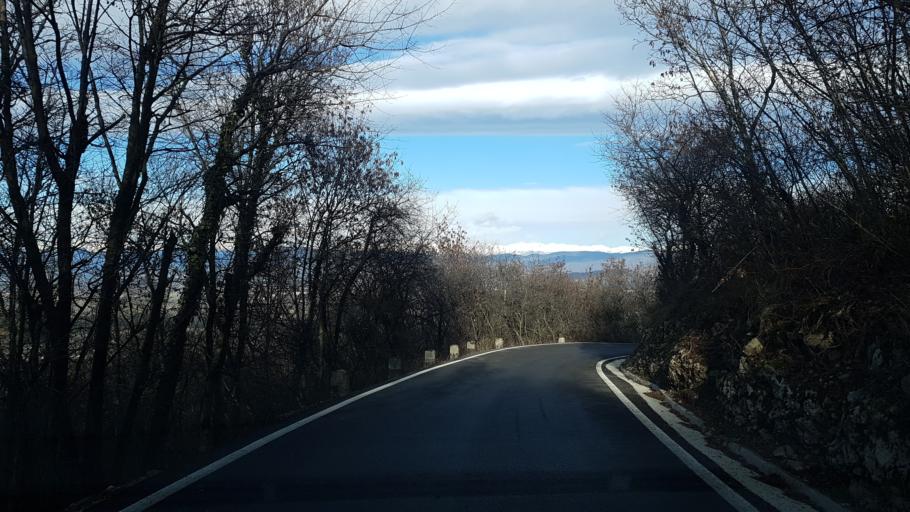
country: IT
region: Friuli Venezia Giulia
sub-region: Provincia di Gorizia
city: Farra d'Isonzo
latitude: 45.8887
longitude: 13.5457
